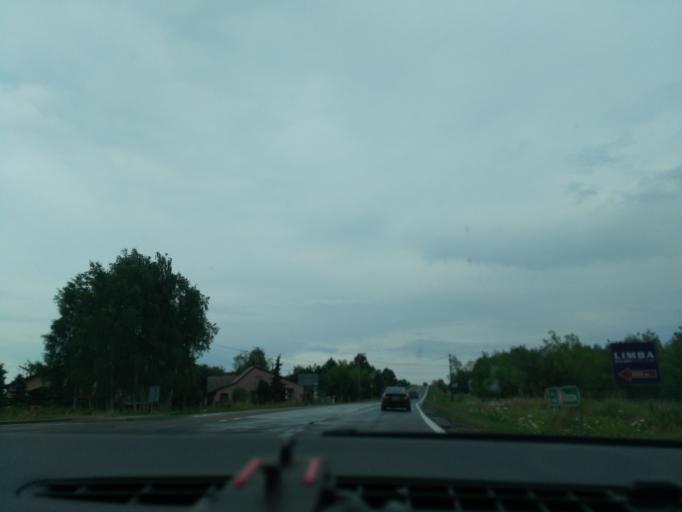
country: PL
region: Subcarpathian Voivodeship
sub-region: Powiat nizanski
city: Nisko
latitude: 50.5081
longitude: 22.1435
